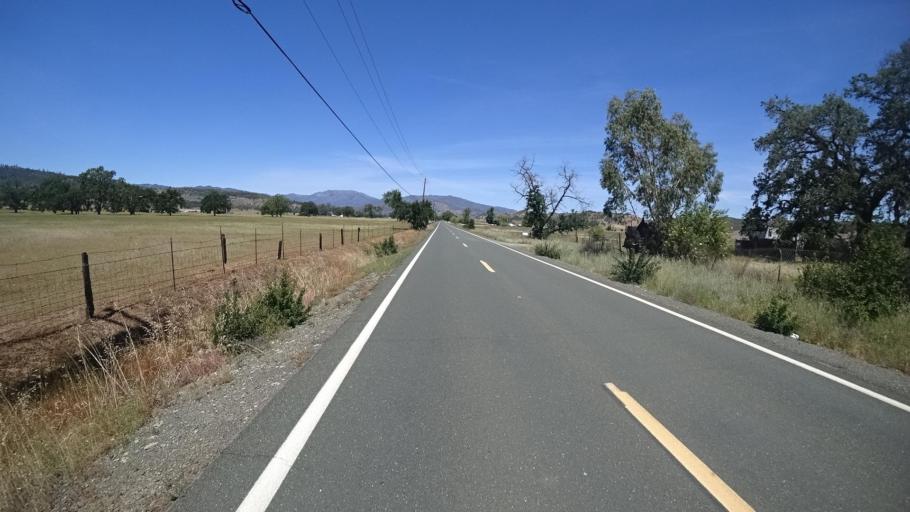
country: US
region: California
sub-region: Lake County
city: Middletown
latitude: 38.7394
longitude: -122.5686
